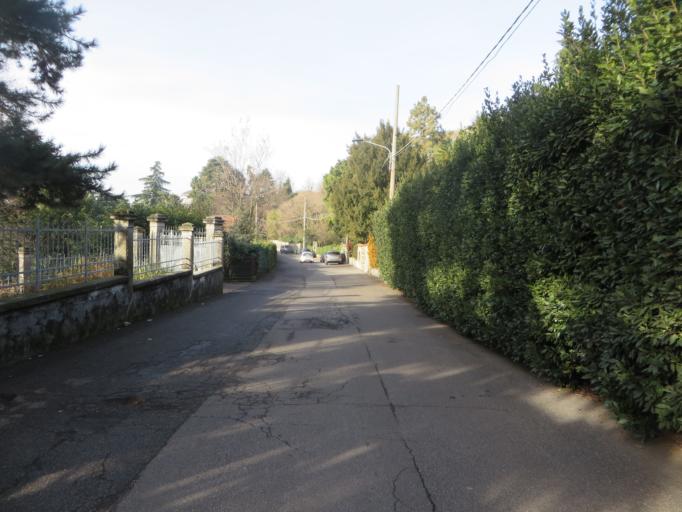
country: IT
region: Lombardy
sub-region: Provincia di Brescia
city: Brescia
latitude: 45.5344
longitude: 10.2479
